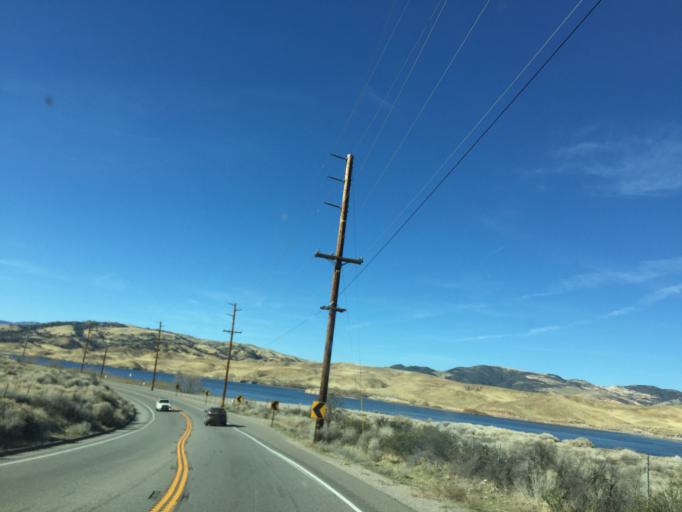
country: US
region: California
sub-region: Kern County
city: Lebec
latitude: 34.7675
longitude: -118.7372
